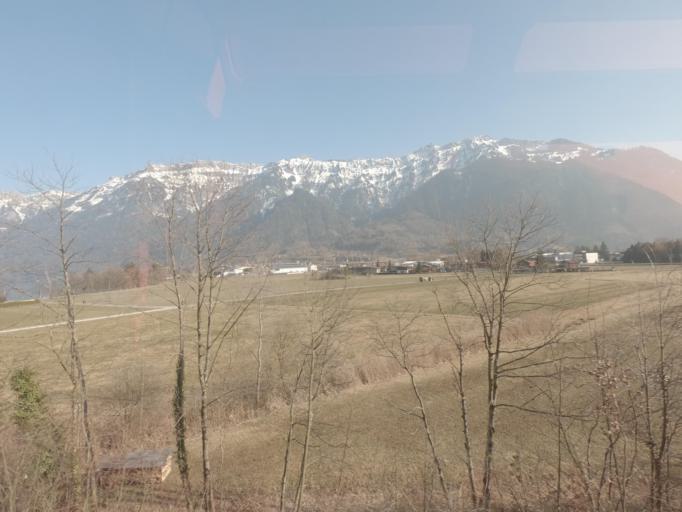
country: CH
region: Bern
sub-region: Interlaken-Oberhasli District
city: Bonigen
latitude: 46.6926
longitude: 7.8810
